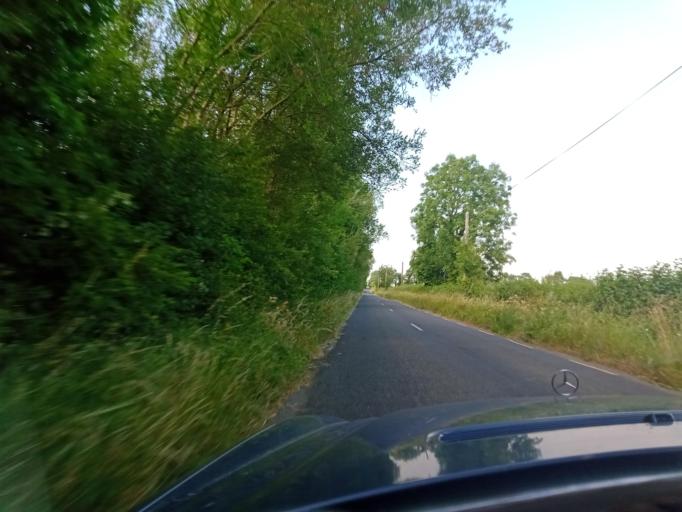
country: IE
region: Leinster
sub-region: Kilkenny
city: Callan
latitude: 52.4919
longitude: -7.3210
